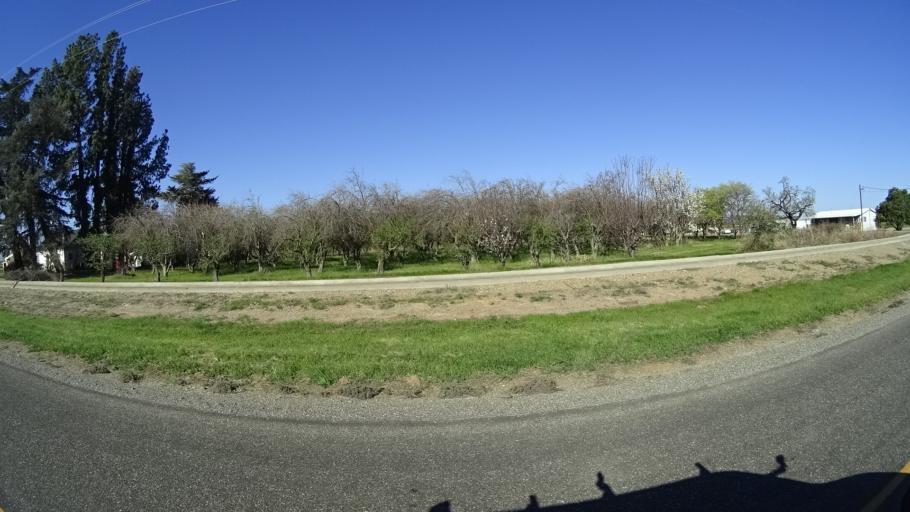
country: US
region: California
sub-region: Glenn County
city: Orland
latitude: 39.7437
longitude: -122.2480
